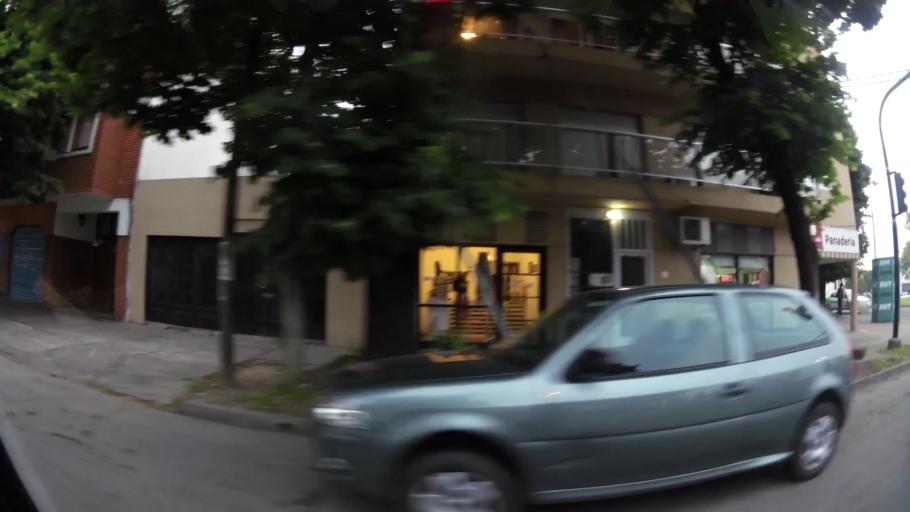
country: AR
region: Buenos Aires
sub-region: Partido de La Plata
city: La Plata
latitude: -34.9120
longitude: -57.9811
